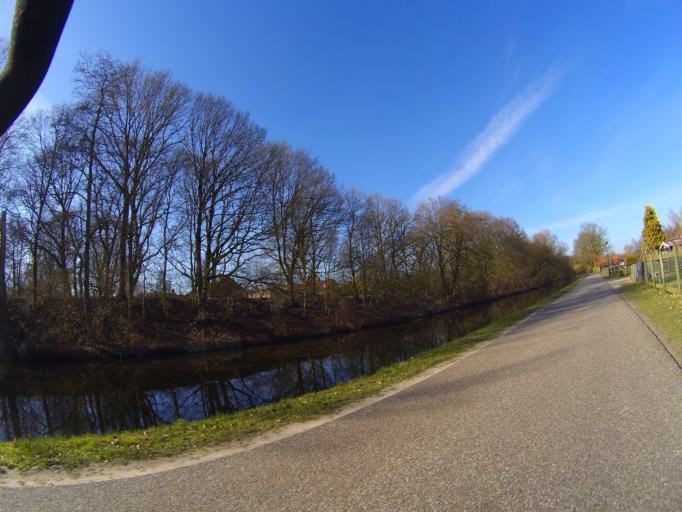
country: NL
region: Utrecht
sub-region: Gemeente Leusden
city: Leusden
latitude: 52.1301
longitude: 5.4469
